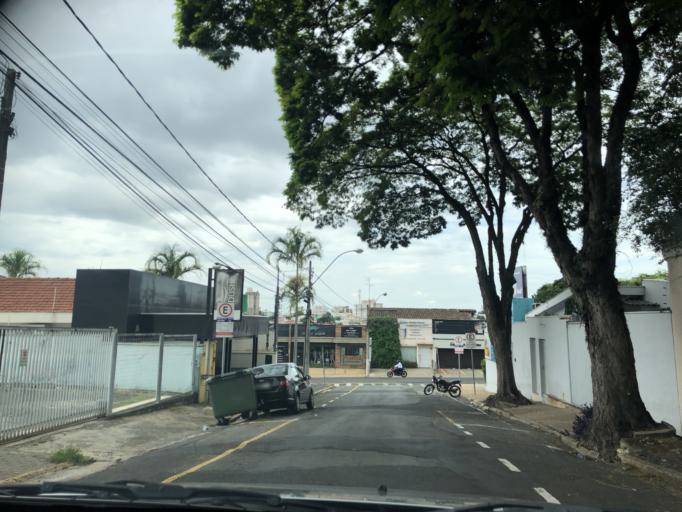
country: BR
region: Sao Paulo
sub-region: Americana
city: Americana
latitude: -22.7428
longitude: -47.3348
